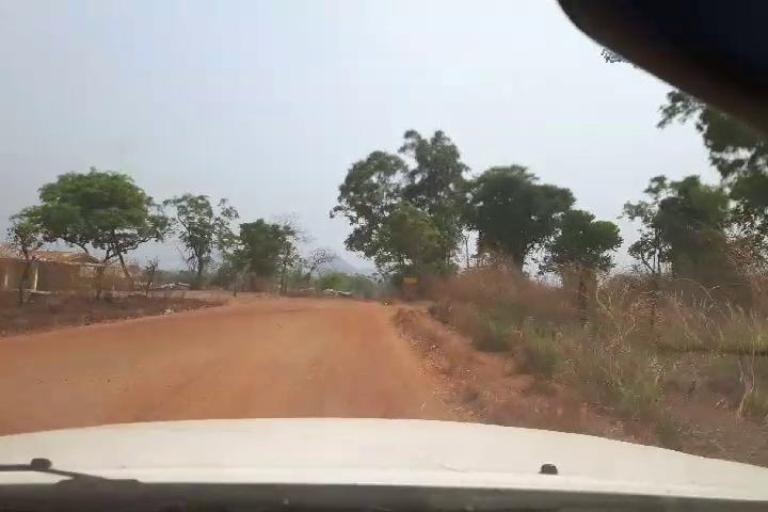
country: SL
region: Northern Province
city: Bumbuna
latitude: 9.0035
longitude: -11.7769
